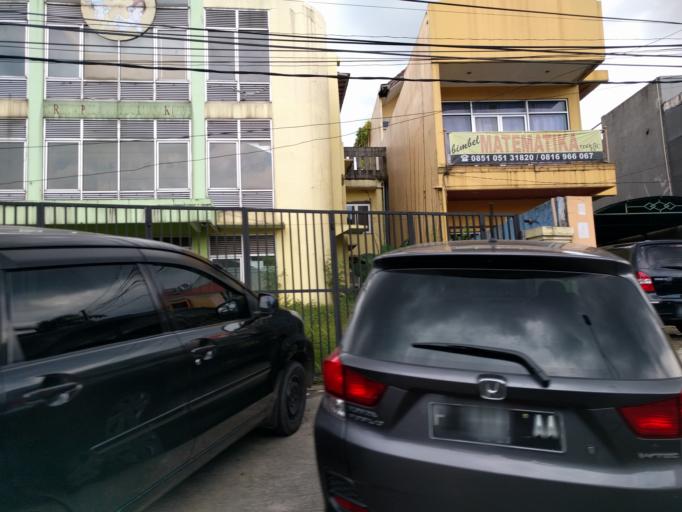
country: ID
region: West Java
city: Bogor
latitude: -6.5818
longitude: 106.8167
